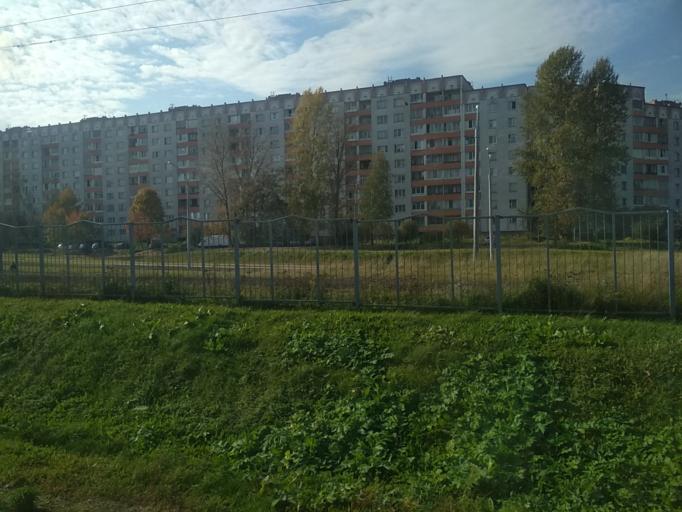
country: BY
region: Minsk
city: Syenitsa
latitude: 53.8533
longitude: 27.5570
